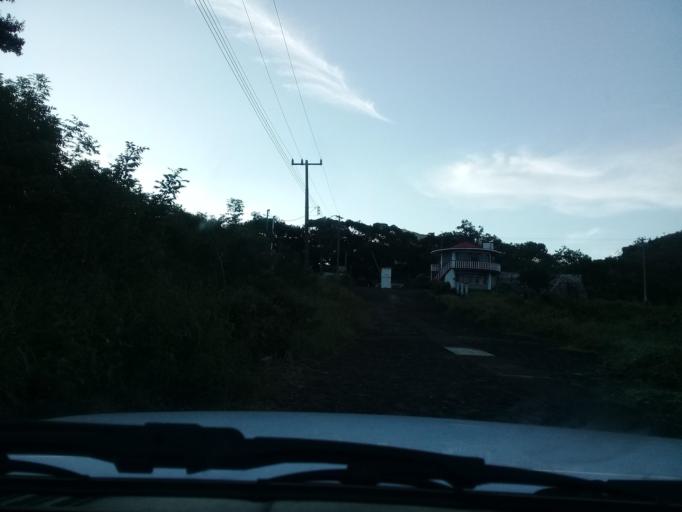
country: MX
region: Veracruz
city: Catemaco
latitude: 18.4375
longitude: -95.0877
